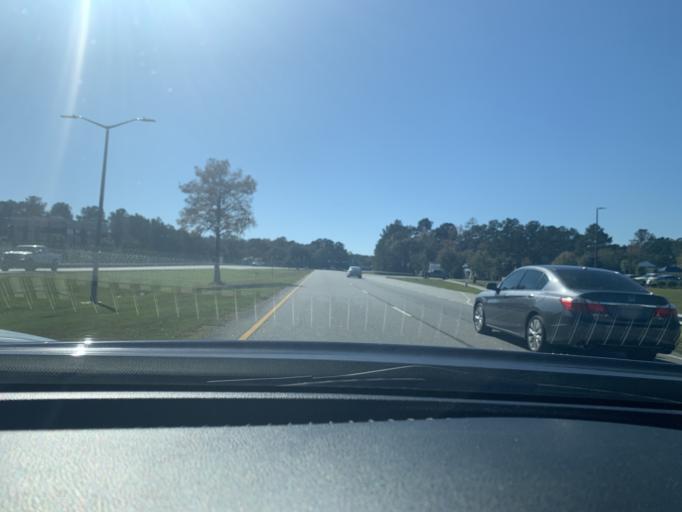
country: US
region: Georgia
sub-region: Chatham County
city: Pooler
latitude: 32.1329
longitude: -81.2559
